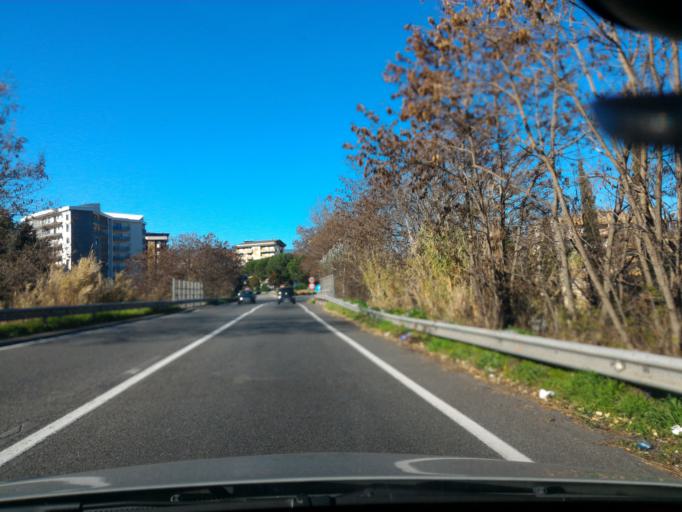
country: IT
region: Calabria
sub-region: Provincia di Cosenza
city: Quattromiglia
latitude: 39.3294
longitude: 16.2484
